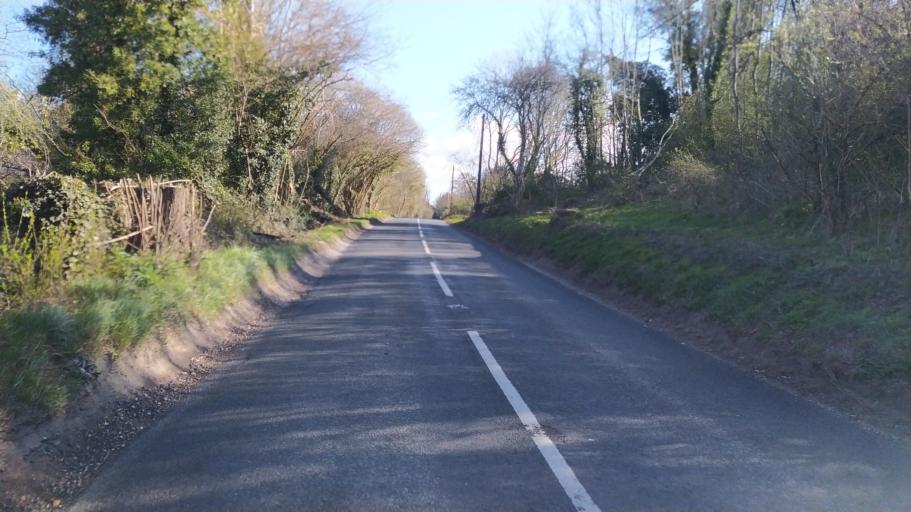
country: GB
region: England
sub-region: Hampshire
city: Abbotts Ann
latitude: 51.1284
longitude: -1.4798
